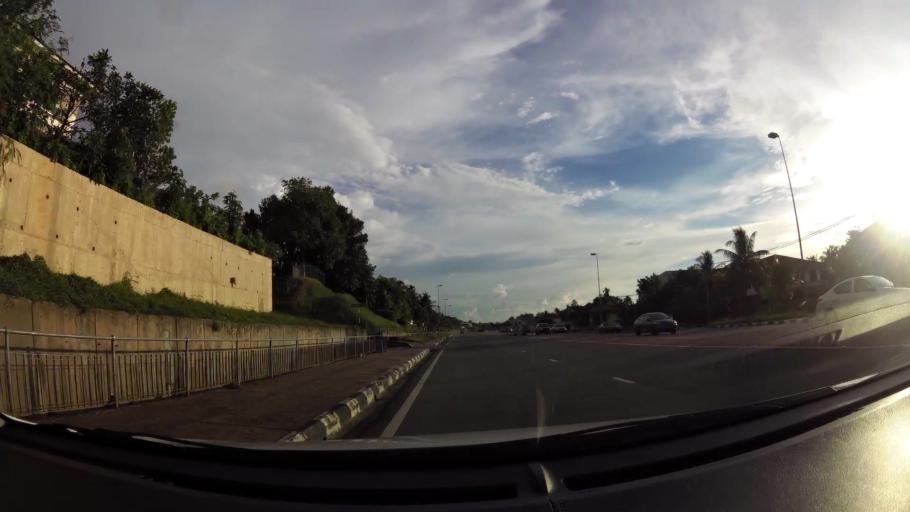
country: BN
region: Brunei and Muara
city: Bandar Seri Begawan
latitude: 4.9807
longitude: 114.9891
